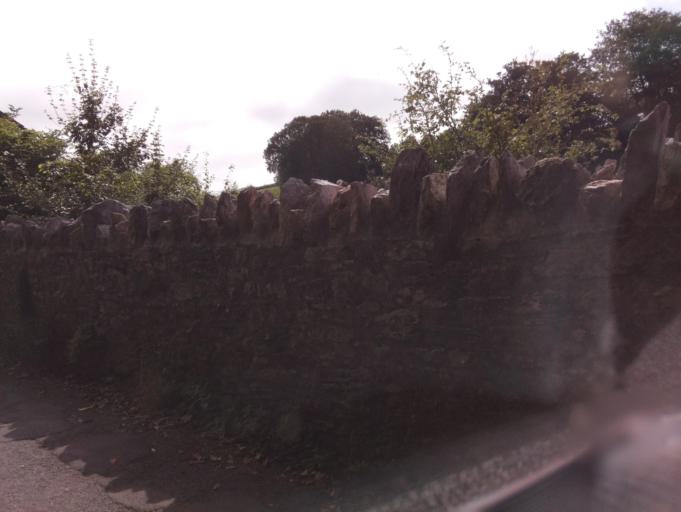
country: GB
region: England
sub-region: Borough of Torbay
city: Paignton
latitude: 50.3954
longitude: -3.5698
